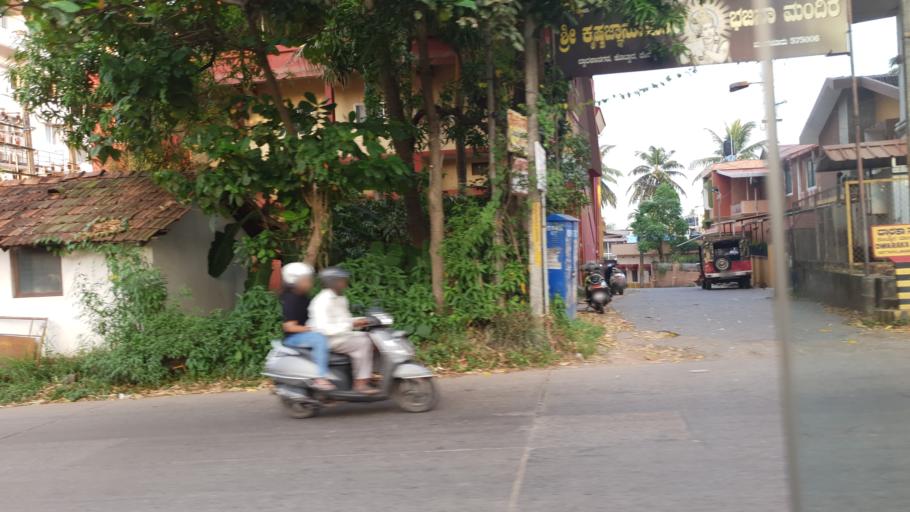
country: IN
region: Karnataka
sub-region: Dakshina Kannada
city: Mangalore
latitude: 12.9073
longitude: 74.8361
